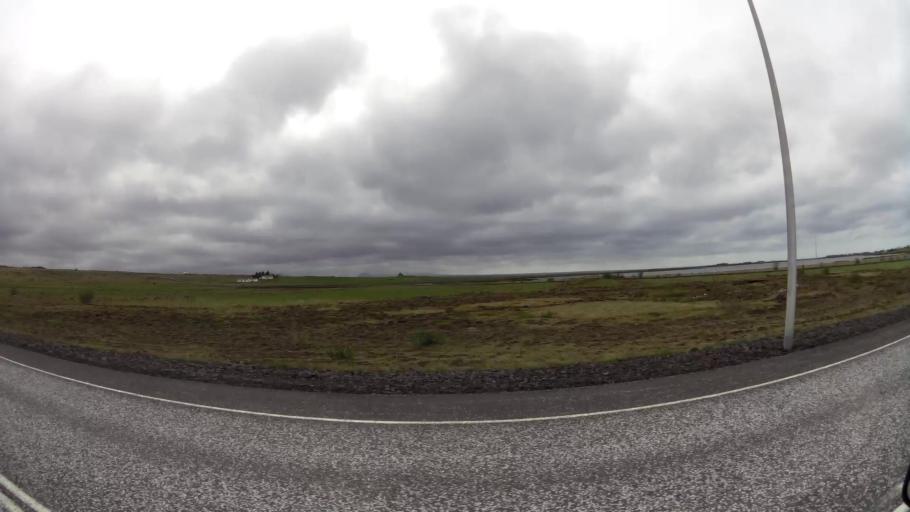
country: IS
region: Capital Region
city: Alftanes
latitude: 64.0957
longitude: -21.9996
